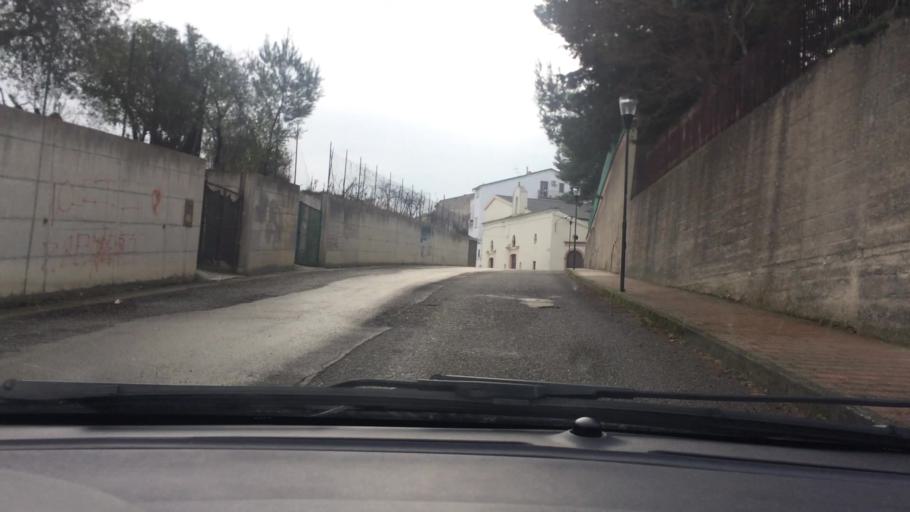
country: IT
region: Basilicate
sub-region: Provincia di Matera
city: San Mauro Forte
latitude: 40.4882
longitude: 16.2460
